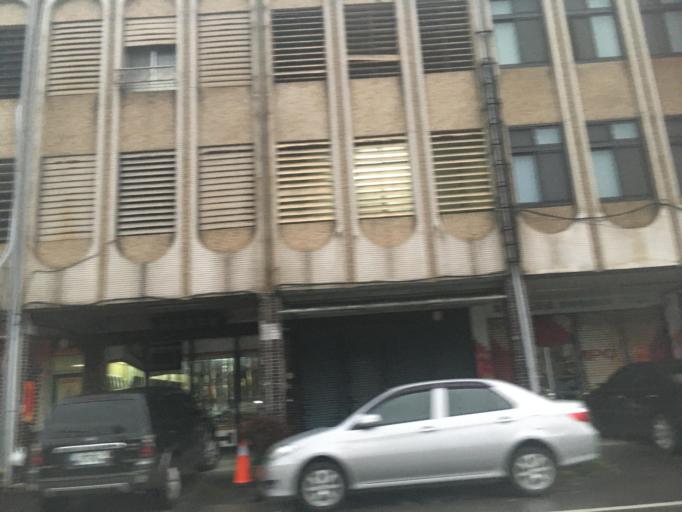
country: TW
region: Taiwan
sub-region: Yilan
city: Yilan
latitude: 24.8581
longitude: 121.8257
